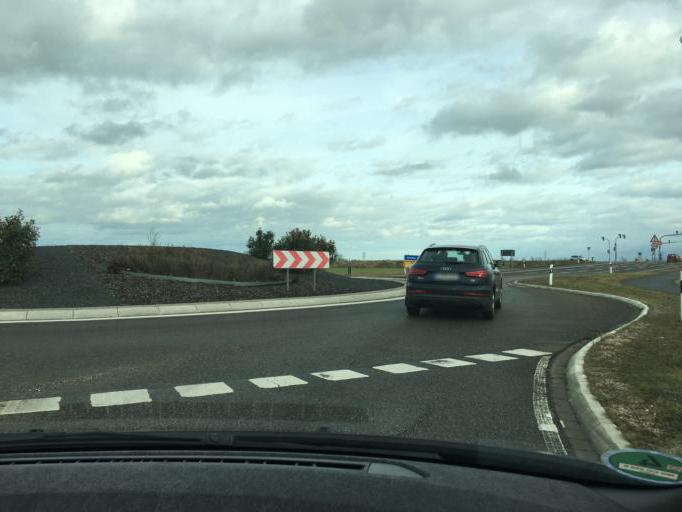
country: DE
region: North Rhine-Westphalia
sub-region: Regierungsbezirk Koln
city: Euskirchen
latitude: 50.6362
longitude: 6.7929
